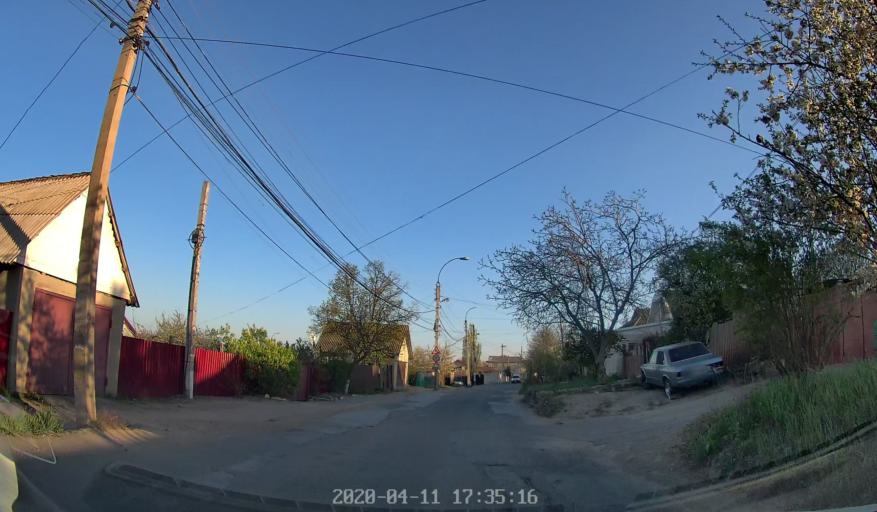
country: MD
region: Laloveni
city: Ialoveni
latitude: 46.9909
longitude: 28.8037
